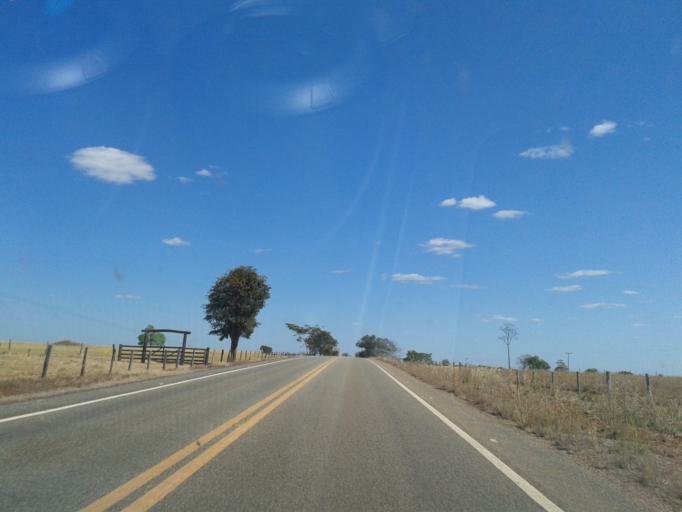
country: BR
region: Goias
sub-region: Sao Miguel Do Araguaia
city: Sao Miguel do Araguaia
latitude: -13.4036
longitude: -50.2605
